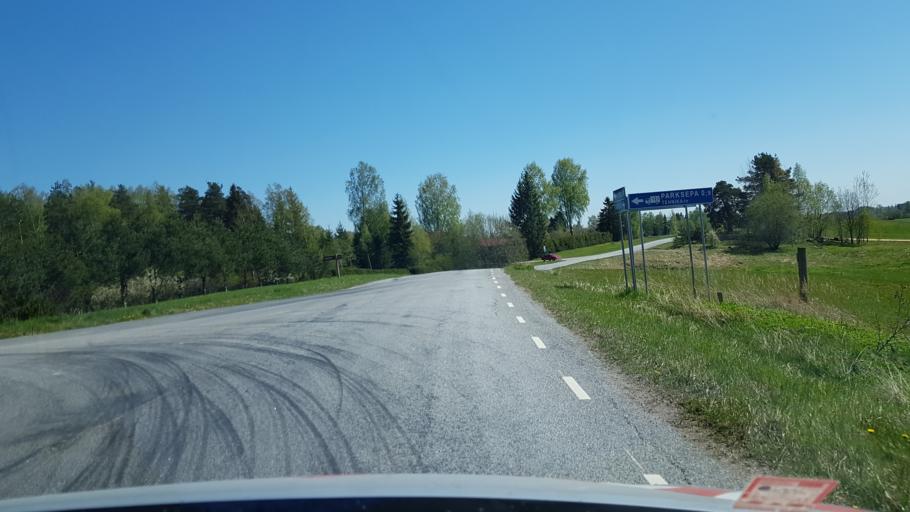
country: EE
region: Vorumaa
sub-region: Voru linn
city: Voru
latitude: 57.9079
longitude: 26.9755
